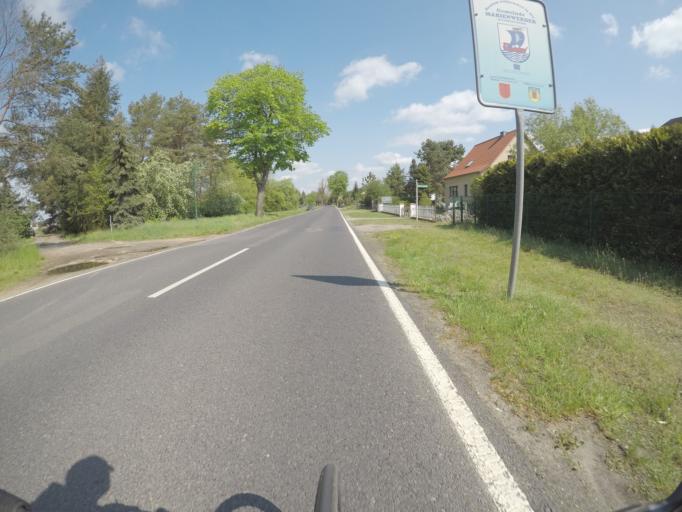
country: DE
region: Brandenburg
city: Marienwerder
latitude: 52.8200
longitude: 13.5573
